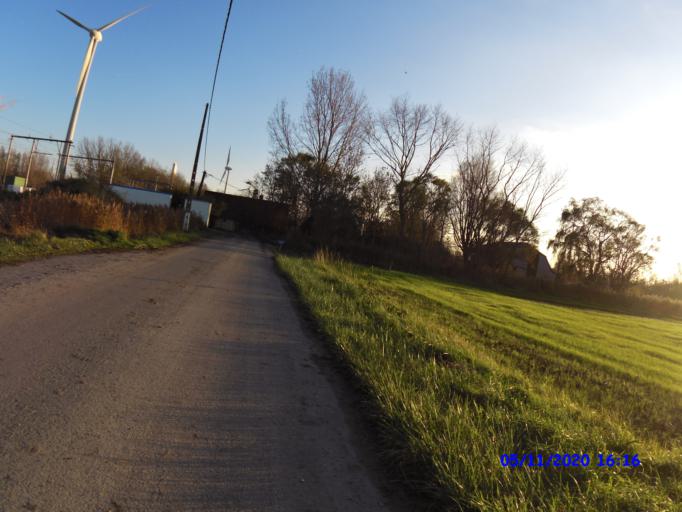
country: BE
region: Flanders
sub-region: Provincie West-Vlaanderen
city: Zuienkerke
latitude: 51.2570
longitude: 3.2035
